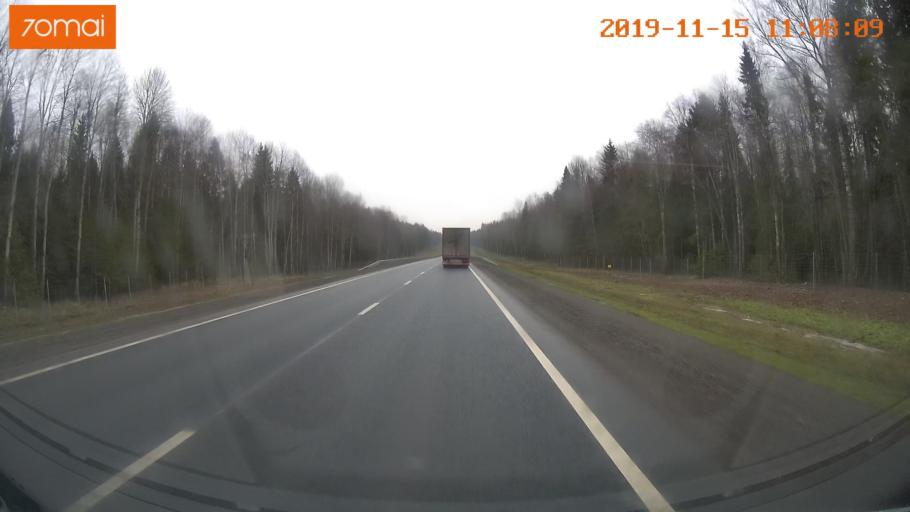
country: RU
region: Vologda
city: Chebsara
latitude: 59.1198
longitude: 39.0673
